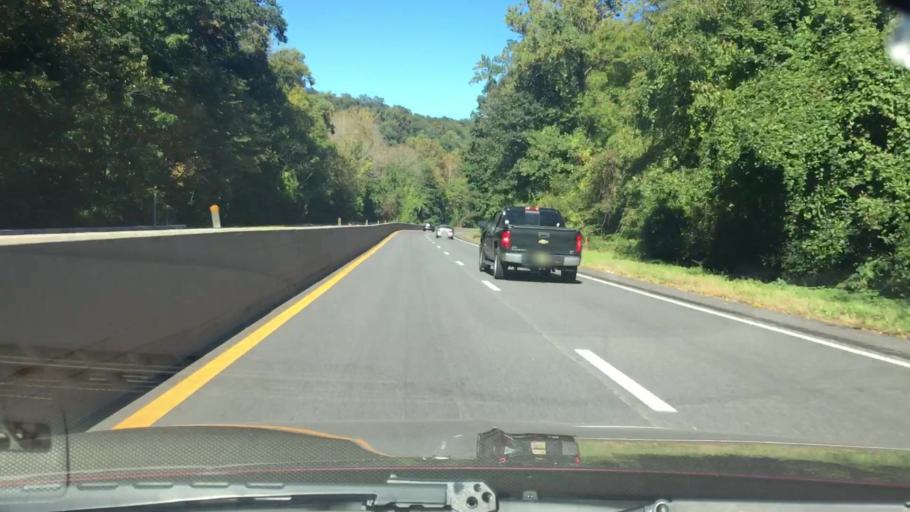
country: US
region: New York
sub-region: Westchester County
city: Pleasantville
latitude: 41.1389
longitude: -73.7926
